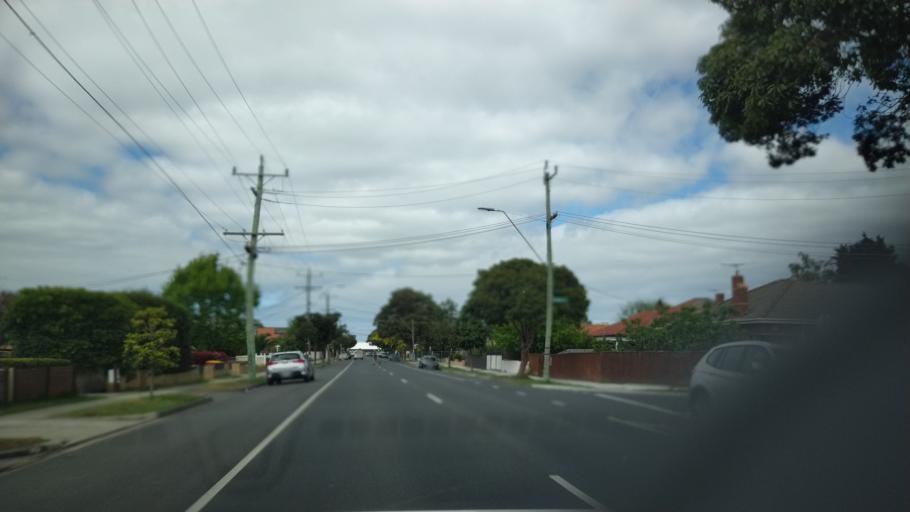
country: AU
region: Victoria
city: Murrumbeena
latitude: -37.9024
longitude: 145.0546
